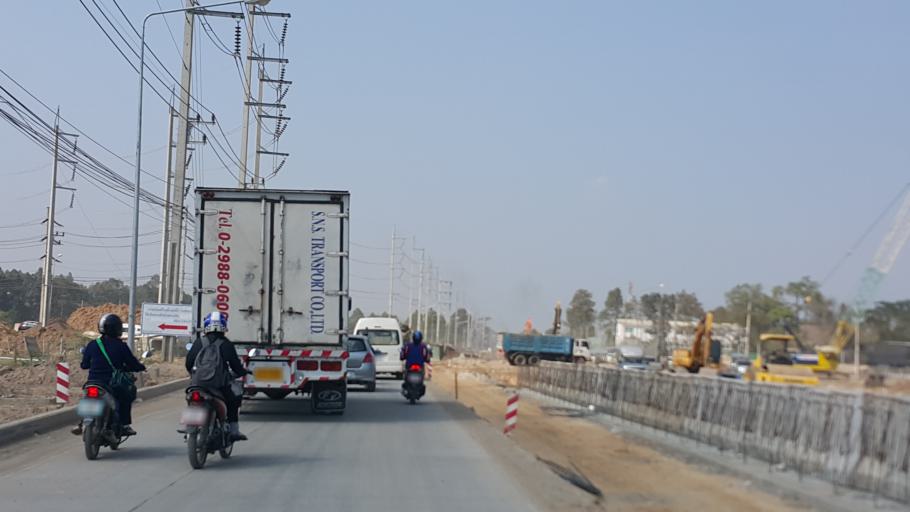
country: TH
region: Chiang Mai
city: Chiang Mai
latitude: 18.8657
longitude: 98.9644
